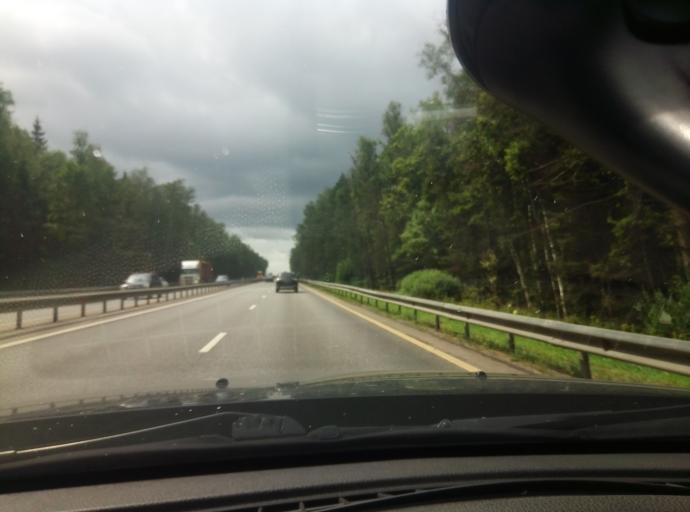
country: RU
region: Kaluga
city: Maloyaroslavets
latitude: 55.0176
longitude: 36.5561
